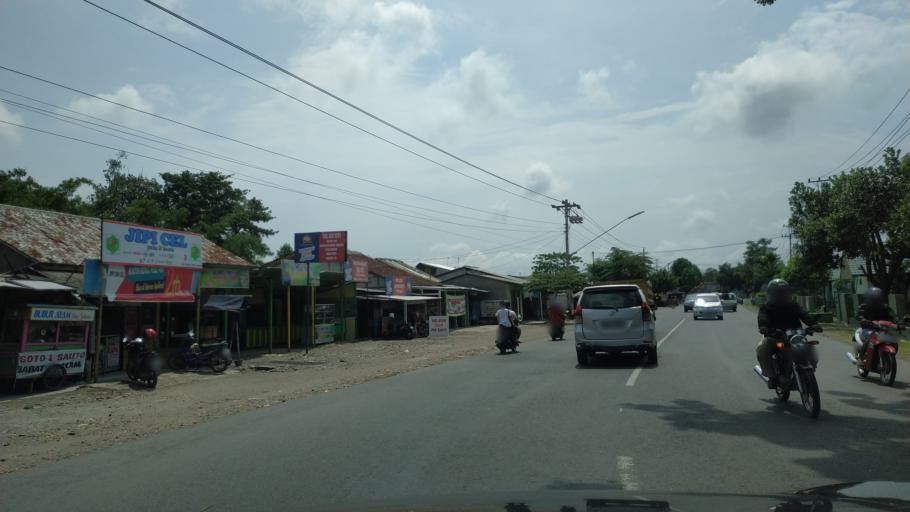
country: ID
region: Central Java
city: Adiwerna
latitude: -6.9436
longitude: 109.1246
